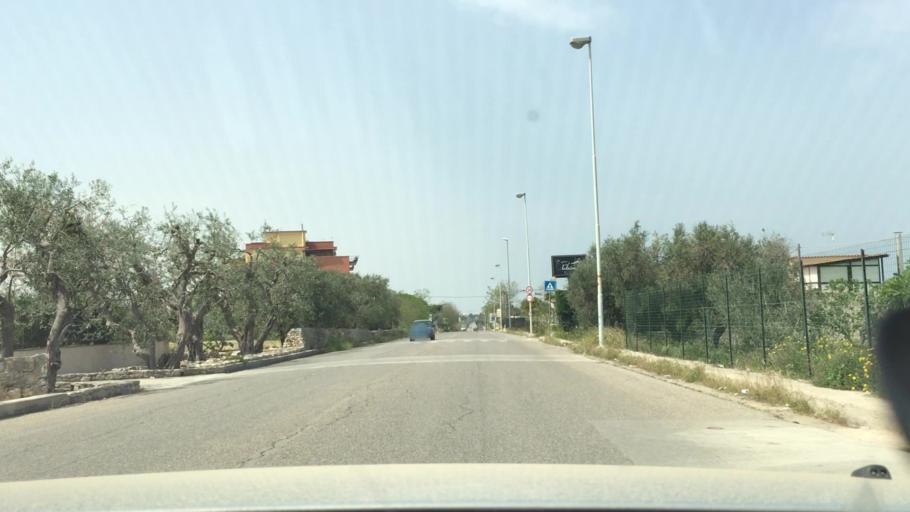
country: IT
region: Apulia
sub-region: Provincia di Barletta - Andria - Trani
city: Capirro
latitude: 41.2562
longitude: 16.4578
